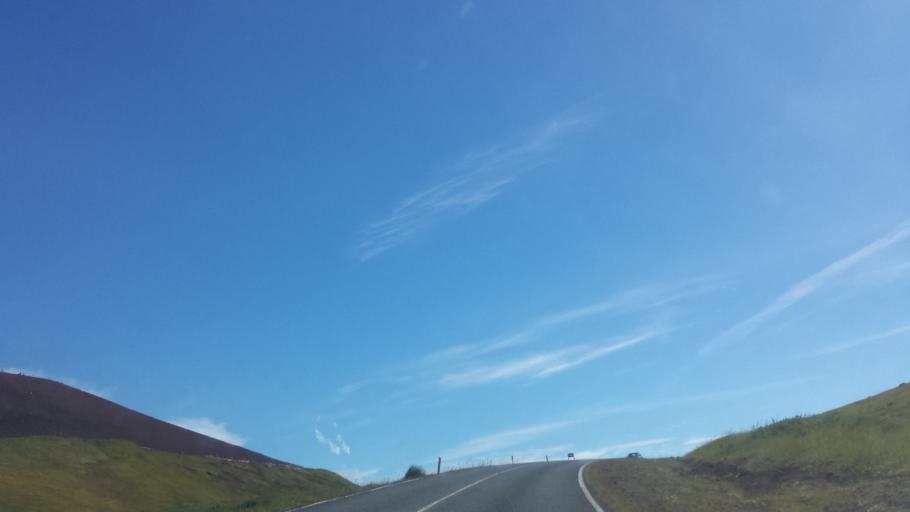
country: IS
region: South
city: Vestmannaeyjar
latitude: 63.4326
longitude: -20.2592
